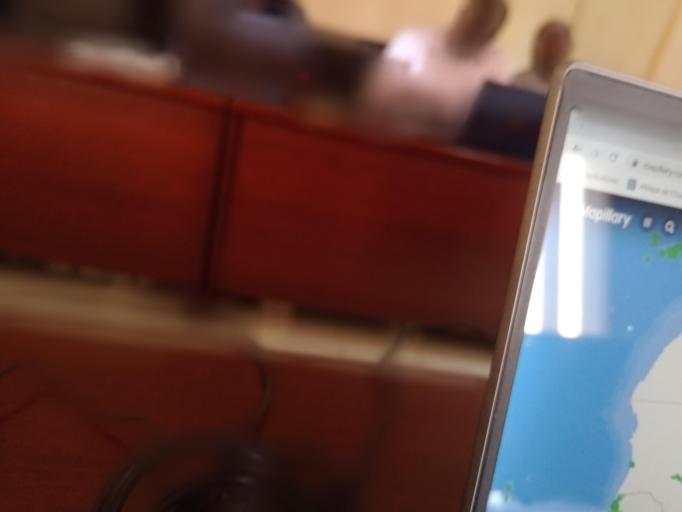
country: BF
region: Centre
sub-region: Kadiogo Province
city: Ouagadougou
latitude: 12.3644
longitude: -1.5187
